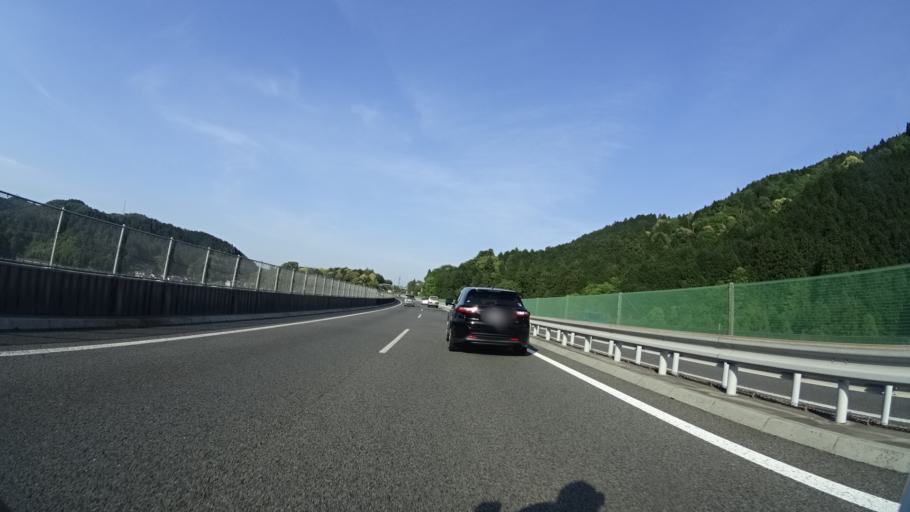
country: JP
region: Ehime
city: Niihama
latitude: 33.9329
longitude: 133.3619
